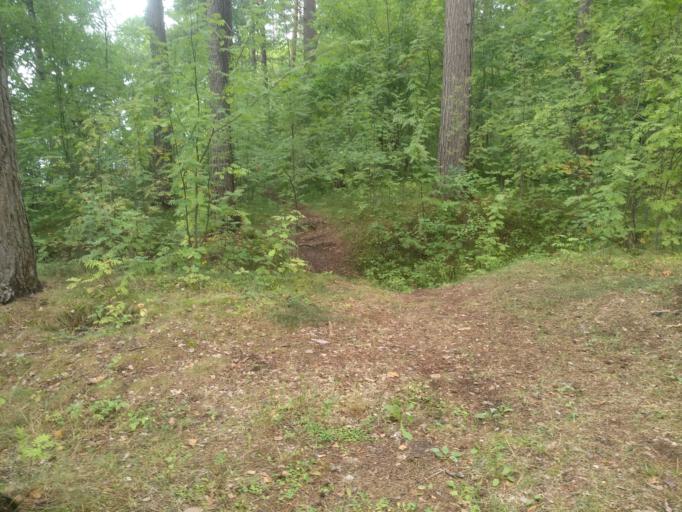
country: RU
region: Leningrad
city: Sapernoye
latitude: 60.6857
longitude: 29.8960
